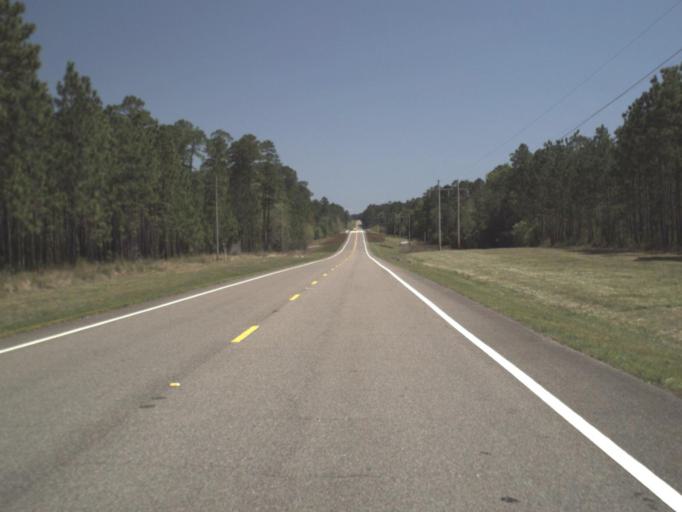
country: US
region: Florida
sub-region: Santa Rosa County
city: Point Baker
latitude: 30.8851
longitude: -86.9647
